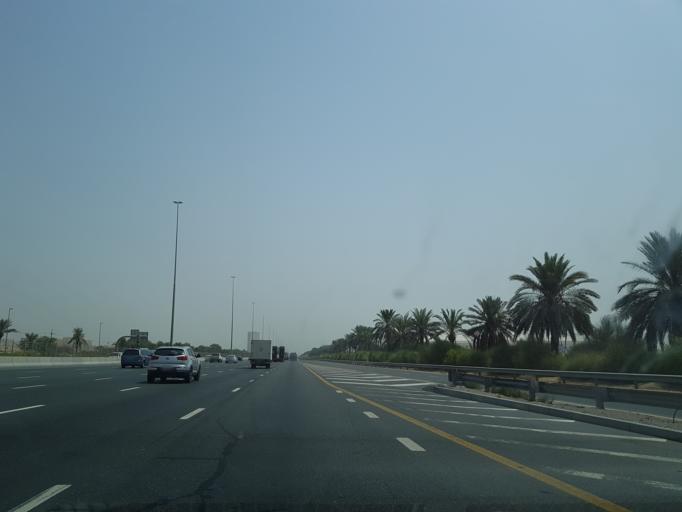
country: AE
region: Dubai
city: Dubai
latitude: 25.0776
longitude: 55.3090
